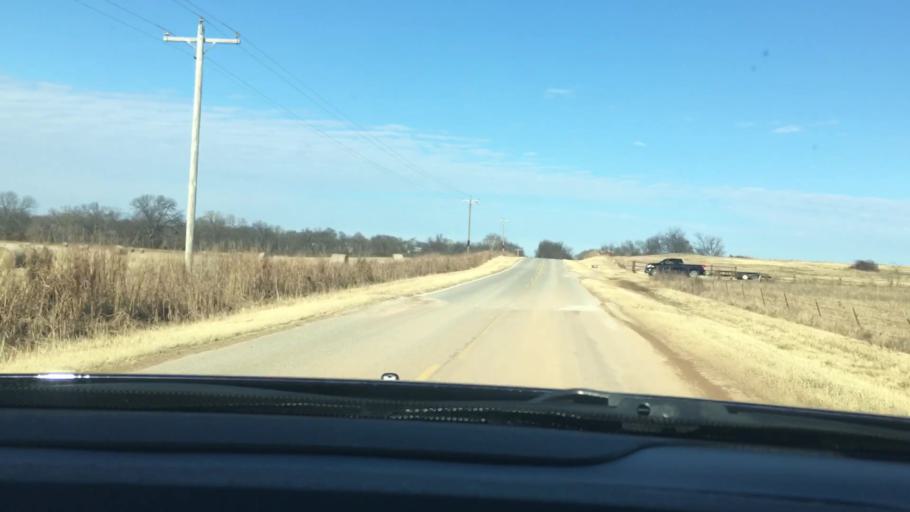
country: US
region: Oklahoma
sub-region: Garvin County
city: Wynnewood
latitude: 34.7177
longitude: -97.1254
